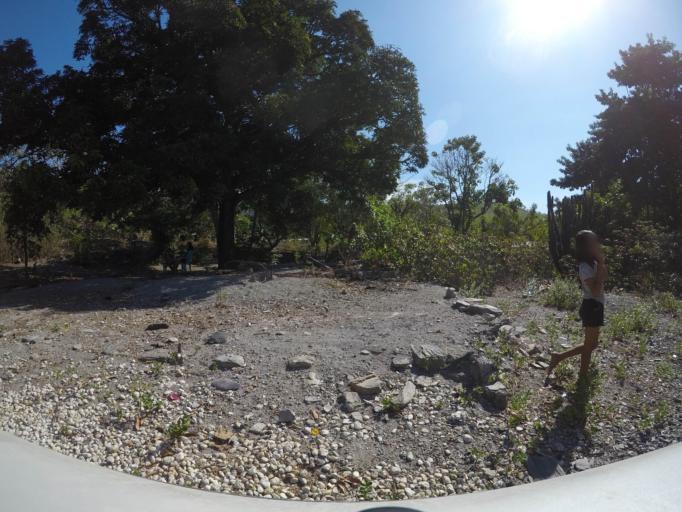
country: TL
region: Liquica
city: Maubara
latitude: -8.6150
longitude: 125.2072
